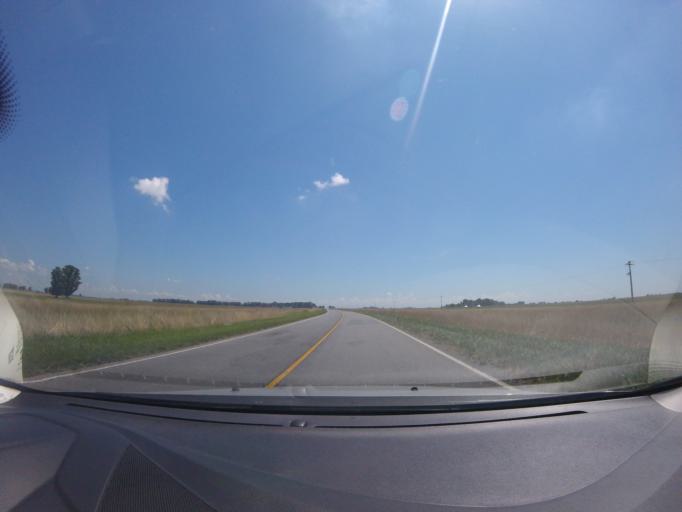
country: AR
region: Buenos Aires
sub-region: Partido de Rauch
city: Rauch
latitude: -36.5961
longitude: -59.0566
